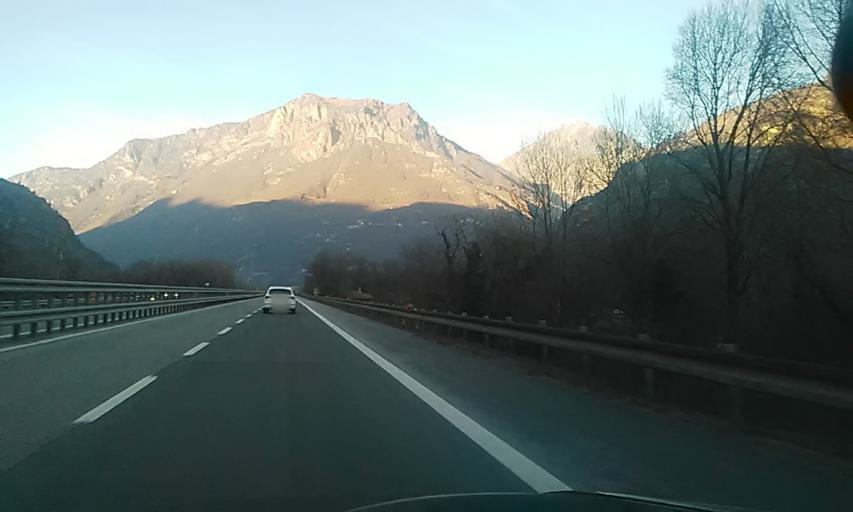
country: IT
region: Piedmont
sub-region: Provincia di Torino
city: Carema
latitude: 45.5764
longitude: 7.8022
